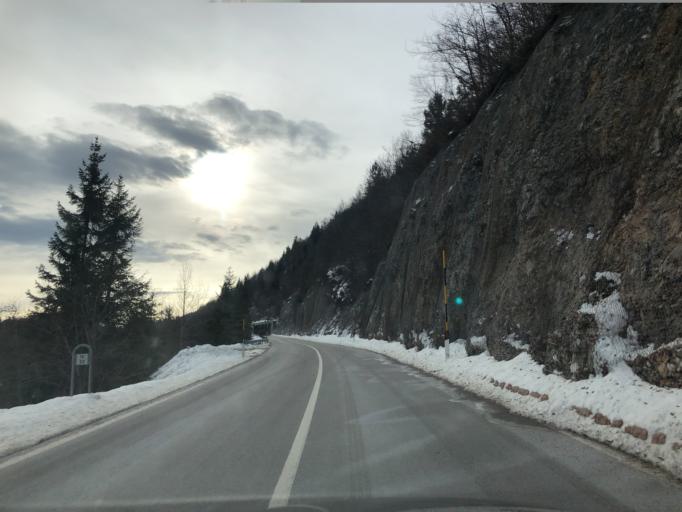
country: IT
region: Trentino-Alto Adige
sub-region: Provincia di Trento
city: Lasino
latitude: 46.0312
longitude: 11.0296
